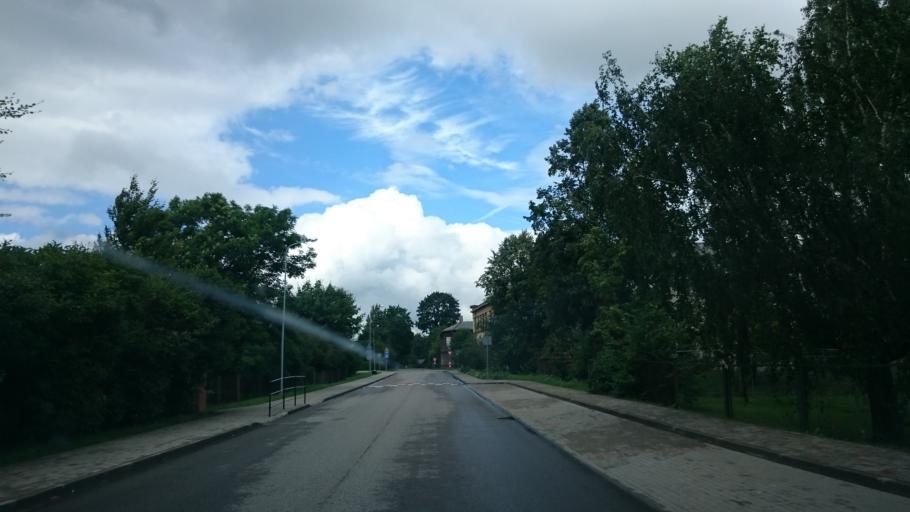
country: LV
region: Aizpute
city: Aizpute
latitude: 56.7208
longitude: 21.6077
